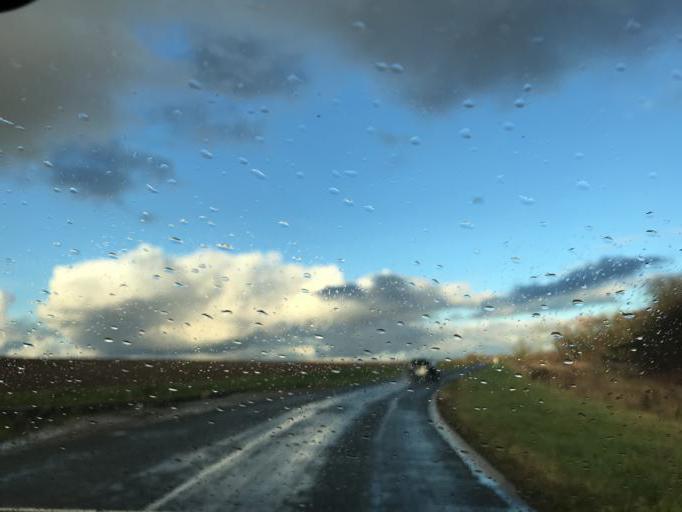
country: FR
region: Ile-de-France
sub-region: Departement de Seine-et-Marne
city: Juilly
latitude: 48.9896
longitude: 2.6941
